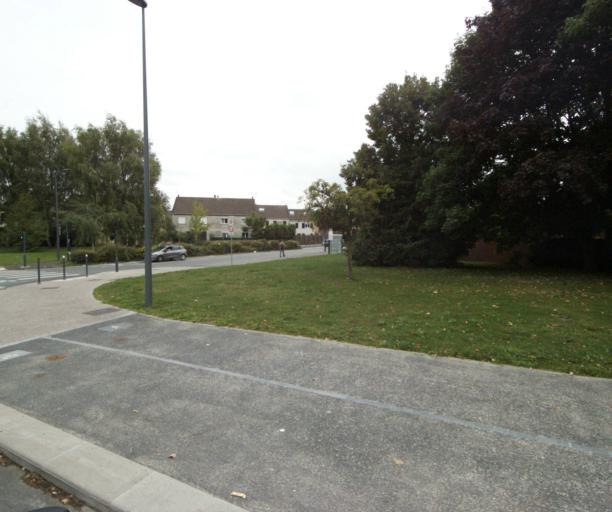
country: FR
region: Nord-Pas-de-Calais
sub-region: Departement du Nord
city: Lezennes
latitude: 50.6179
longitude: 3.1089
